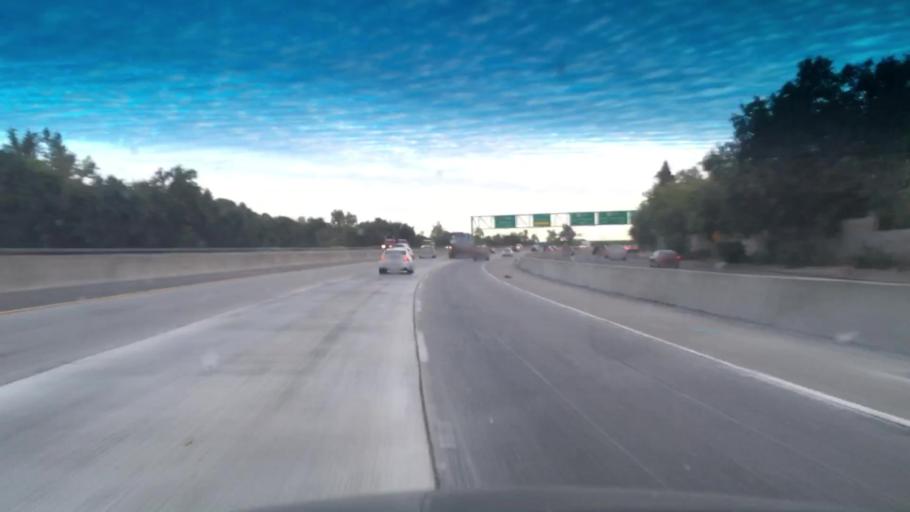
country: US
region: California
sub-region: Yolo County
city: West Sacramento
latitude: 38.5604
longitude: -121.5148
